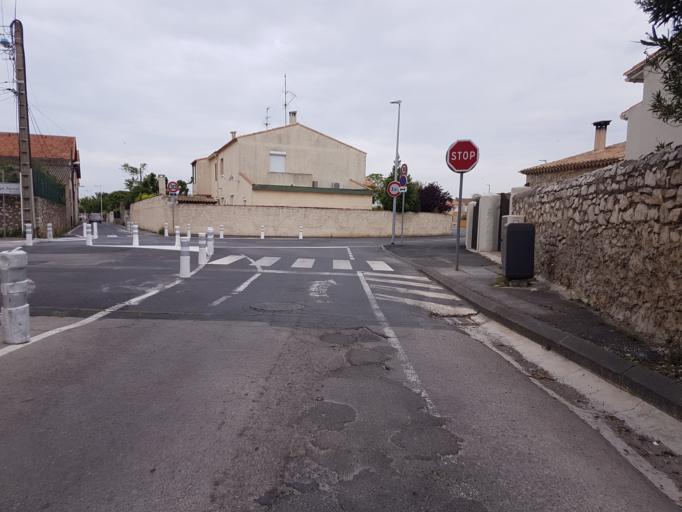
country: FR
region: Languedoc-Roussillon
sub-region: Departement de l'Herault
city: Frontignan
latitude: 43.4436
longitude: 3.7549
